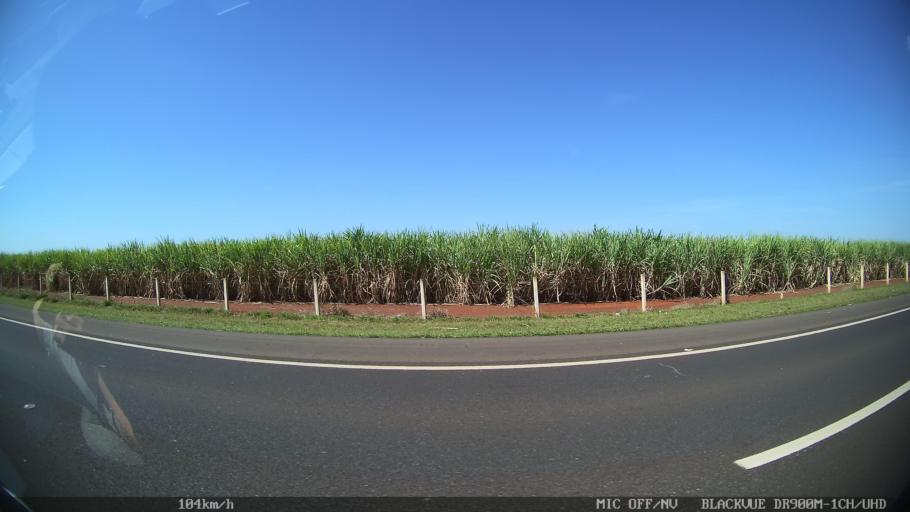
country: BR
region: Sao Paulo
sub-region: Batatais
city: Batatais
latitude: -20.7777
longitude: -47.5473
